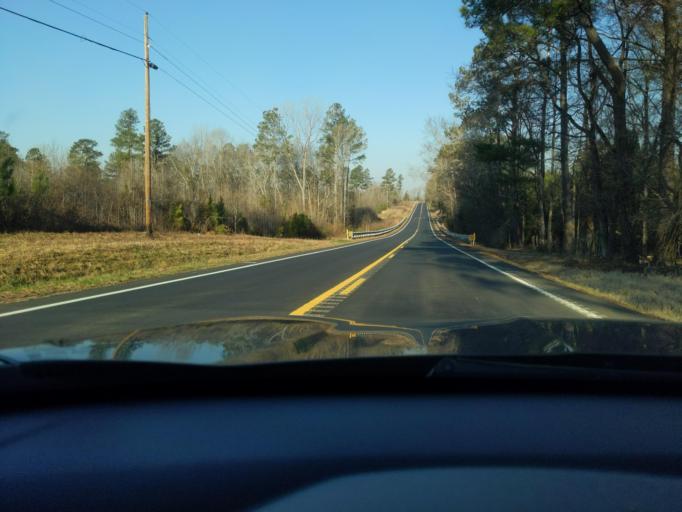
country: US
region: South Carolina
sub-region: Newberry County
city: Newberry
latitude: 34.2014
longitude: -81.8065
